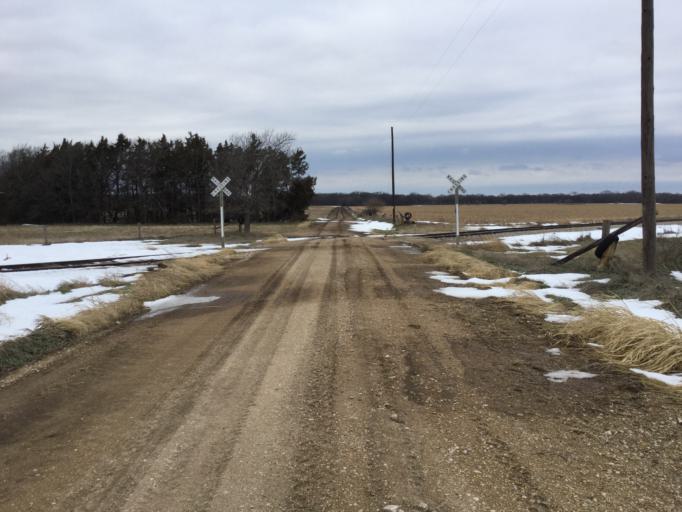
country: US
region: Kansas
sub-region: Lincoln County
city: Lincoln
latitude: 39.1109
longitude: -98.3268
